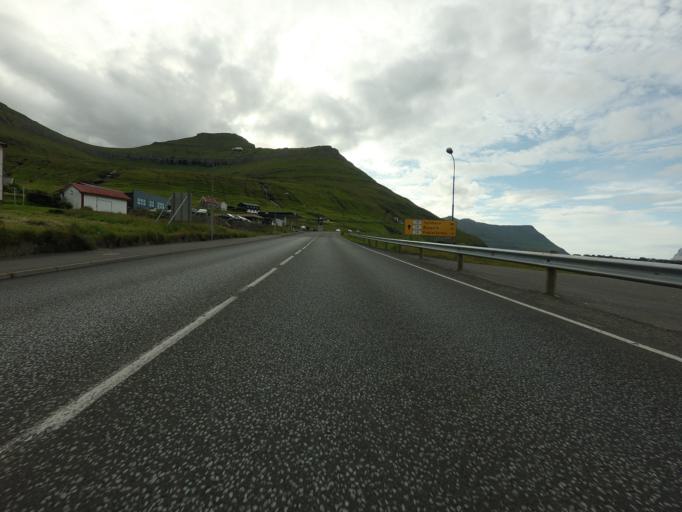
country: FO
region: Eysturoy
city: Eystur
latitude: 62.2131
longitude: -6.7120
